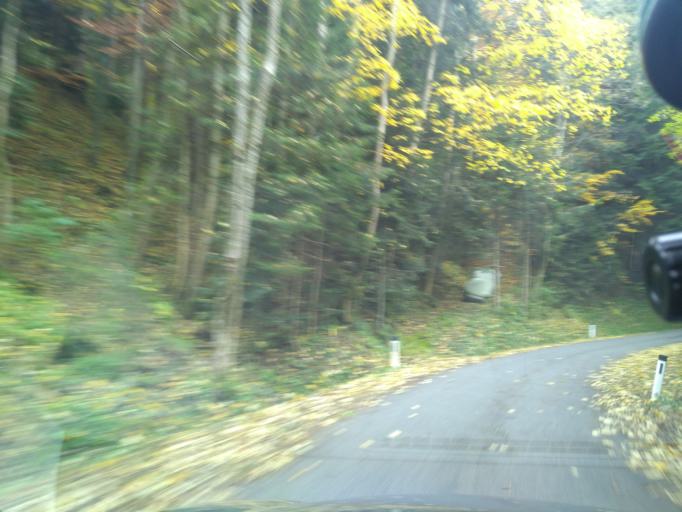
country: AT
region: Styria
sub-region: Politischer Bezirk Leibnitz
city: Leutschach
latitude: 46.6127
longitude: 15.4725
